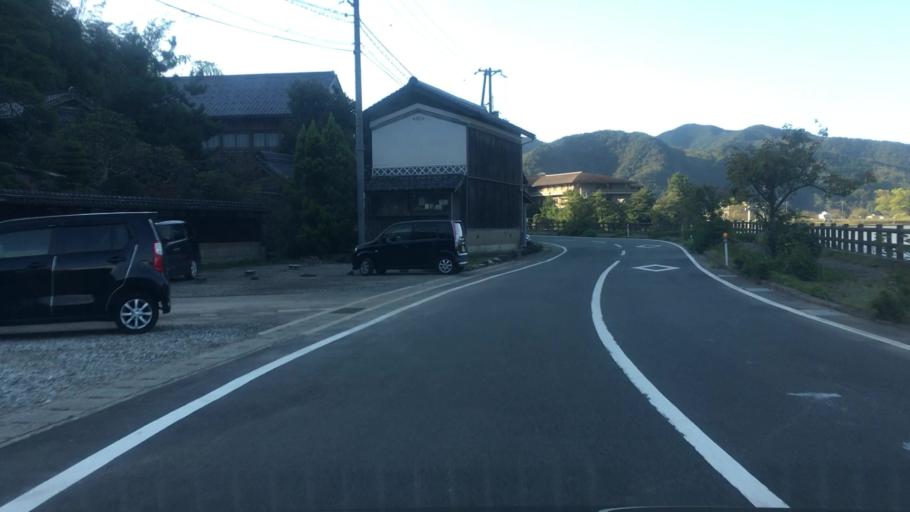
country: JP
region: Hyogo
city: Toyooka
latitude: 35.6184
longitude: 134.8216
